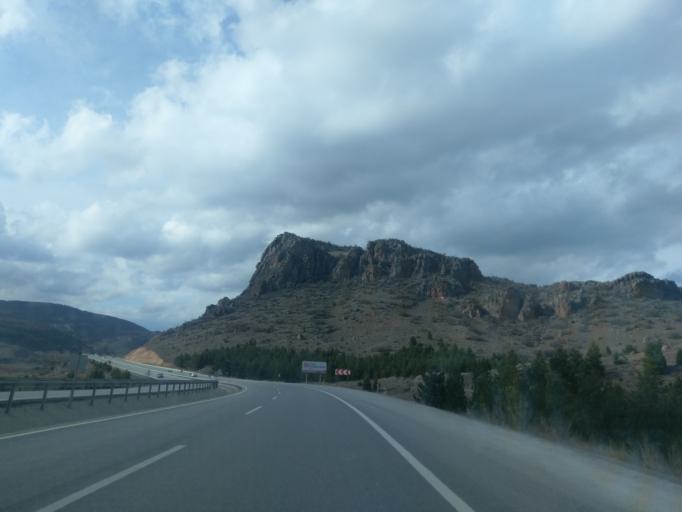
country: TR
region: Kuetahya
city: Sabuncu
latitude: 39.5730
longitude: 30.1027
